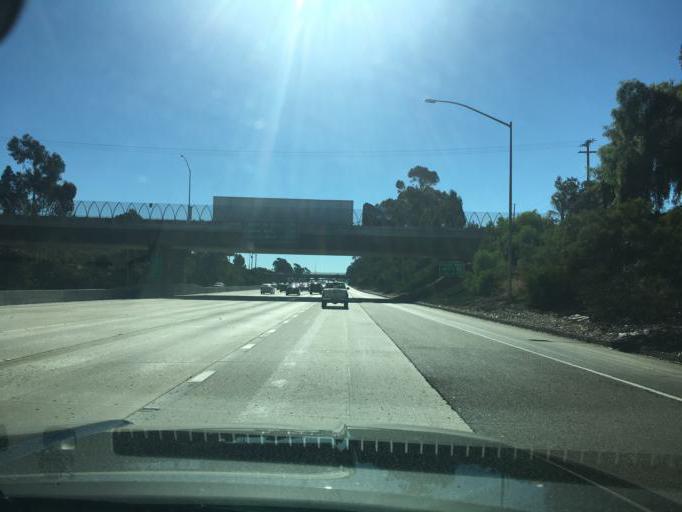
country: US
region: California
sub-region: San Diego County
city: National City
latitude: 32.7010
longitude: -117.0951
